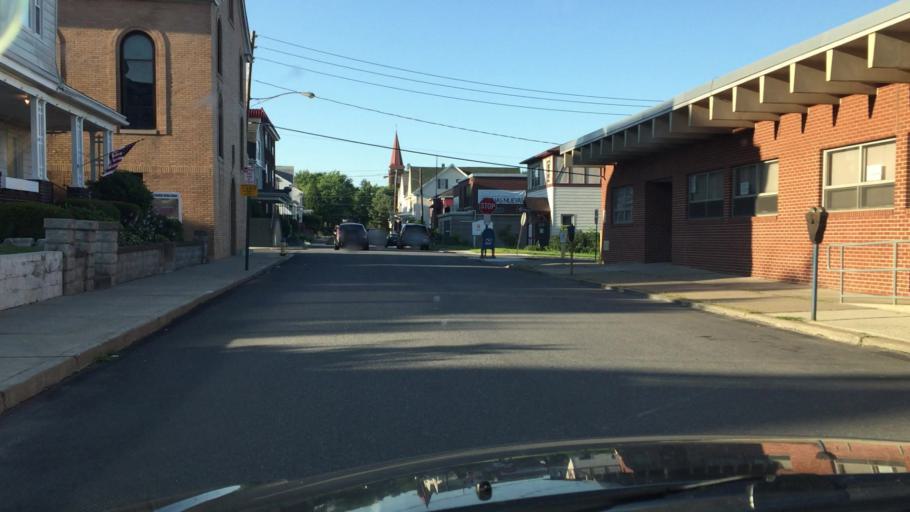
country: US
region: Pennsylvania
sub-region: Luzerne County
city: Hazleton
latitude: 40.9561
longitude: -75.9748
